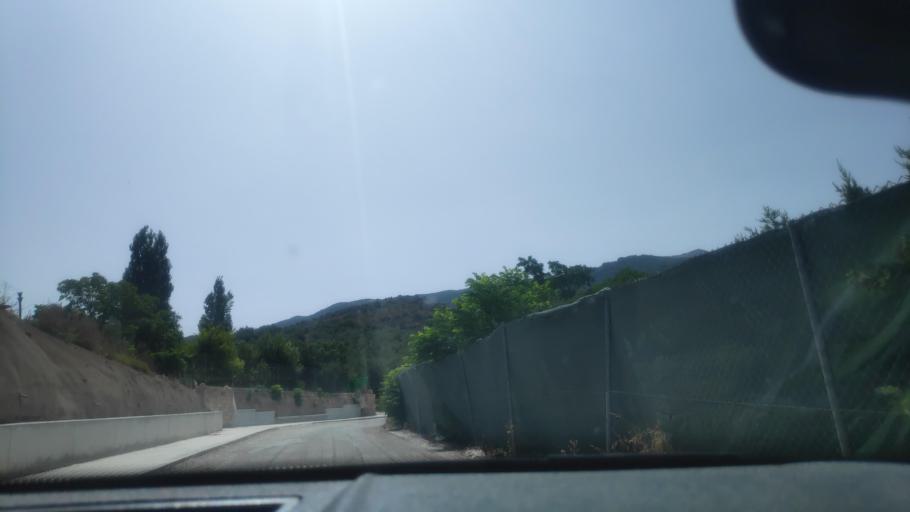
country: ES
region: Andalusia
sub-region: Provincia de Jaen
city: Jodar
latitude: 37.7985
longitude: -3.4101
